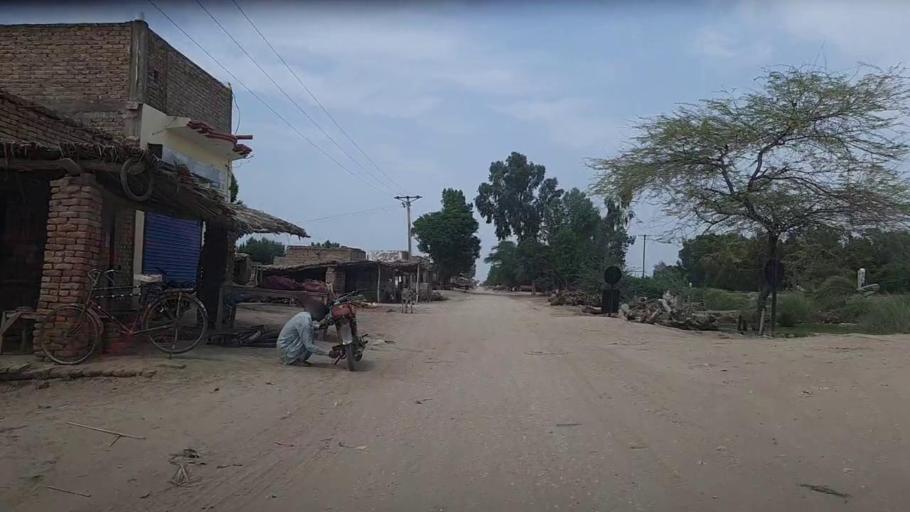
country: PK
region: Sindh
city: Bhiria
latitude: 26.8957
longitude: 68.2865
